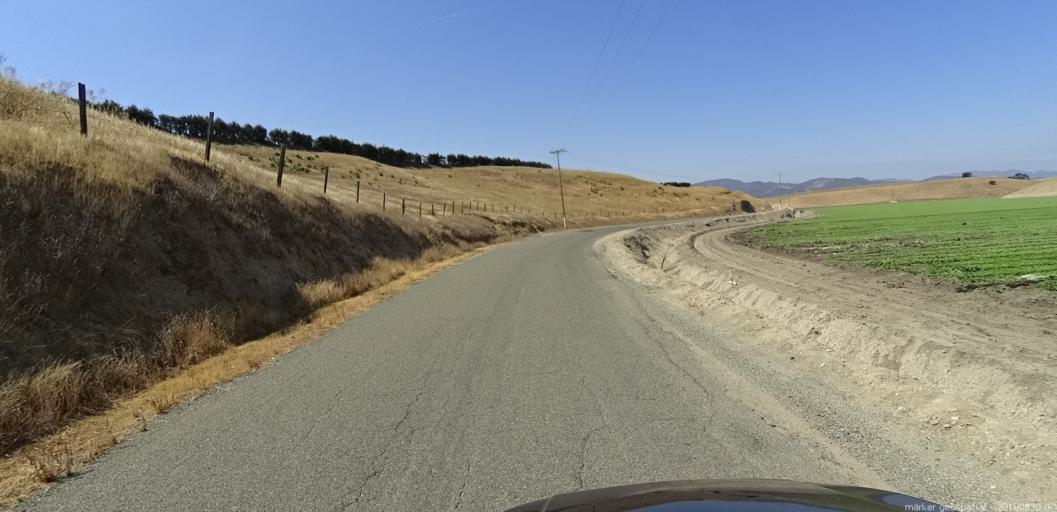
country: US
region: California
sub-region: Monterey County
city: King City
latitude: 36.1089
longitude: -121.0448
